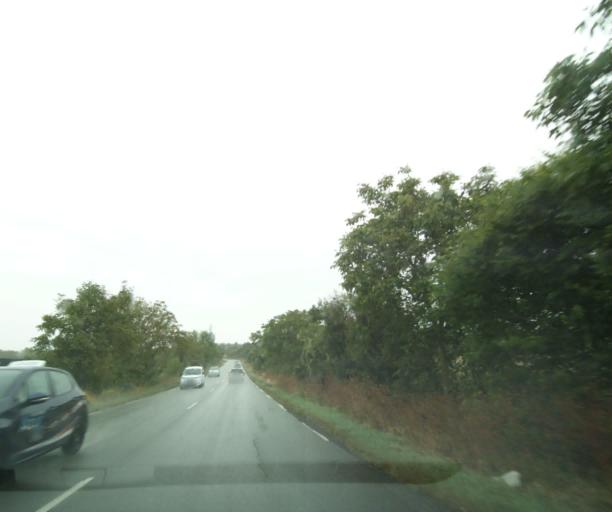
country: FR
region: Auvergne
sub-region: Departement du Puy-de-Dome
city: Cebazat
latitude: 45.8463
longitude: 3.1054
